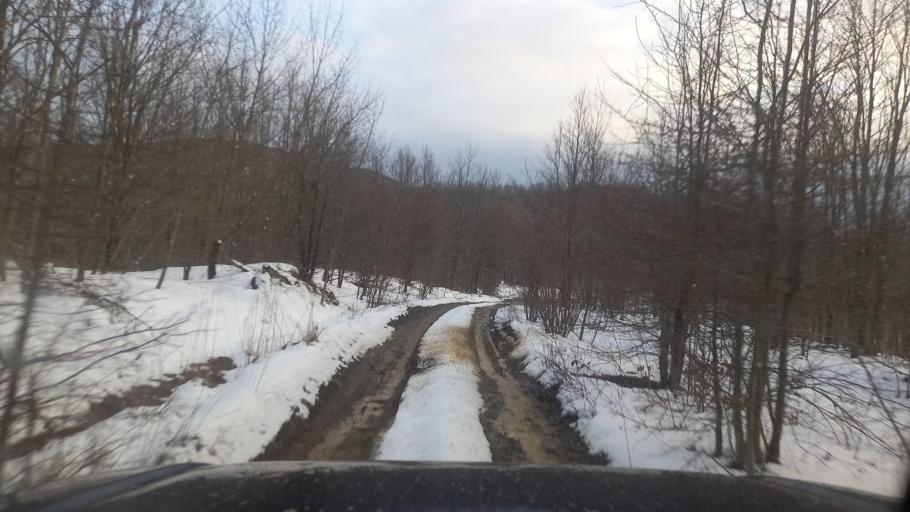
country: RU
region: Krasnodarskiy
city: Smolenskaya
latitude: 44.6800
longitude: 38.7674
